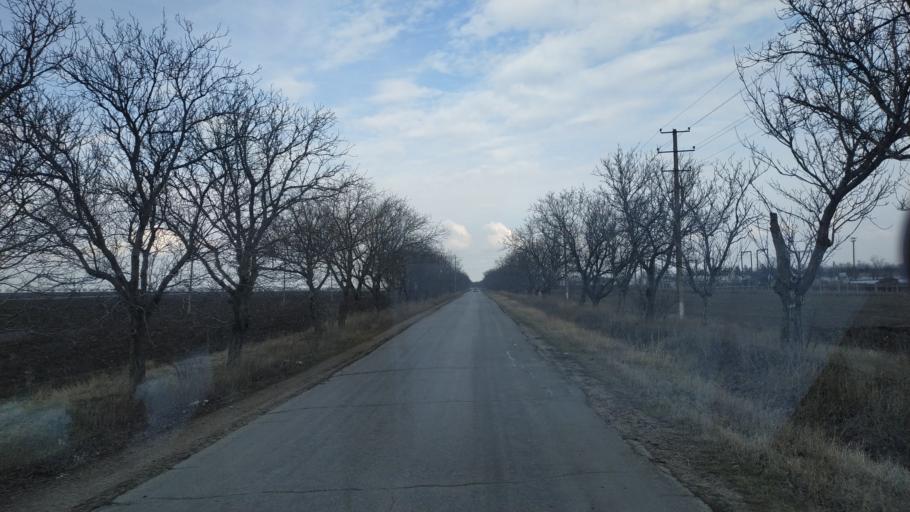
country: MD
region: Anenii Noi
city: Anenii Noi
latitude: 46.9125
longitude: 29.3288
